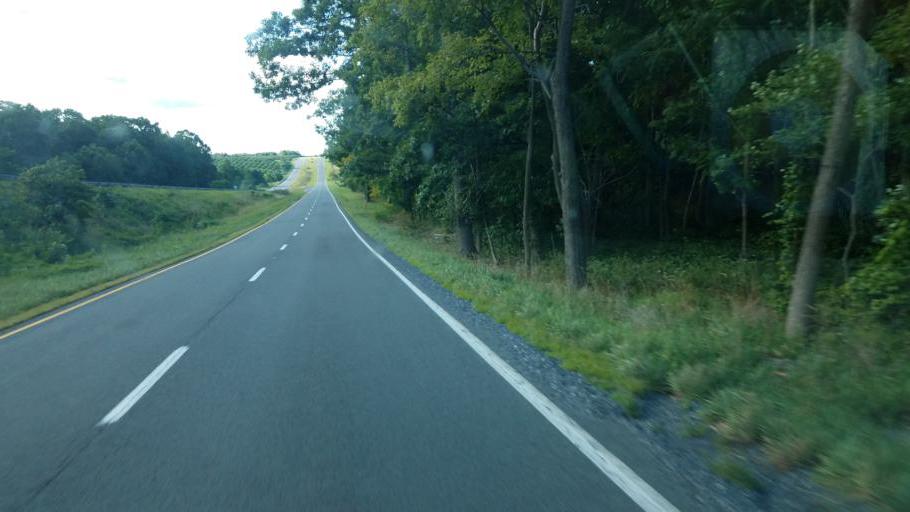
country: US
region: Virginia
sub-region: Frederick County
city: Shawnee Land
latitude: 39.3963
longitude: -78.3077
